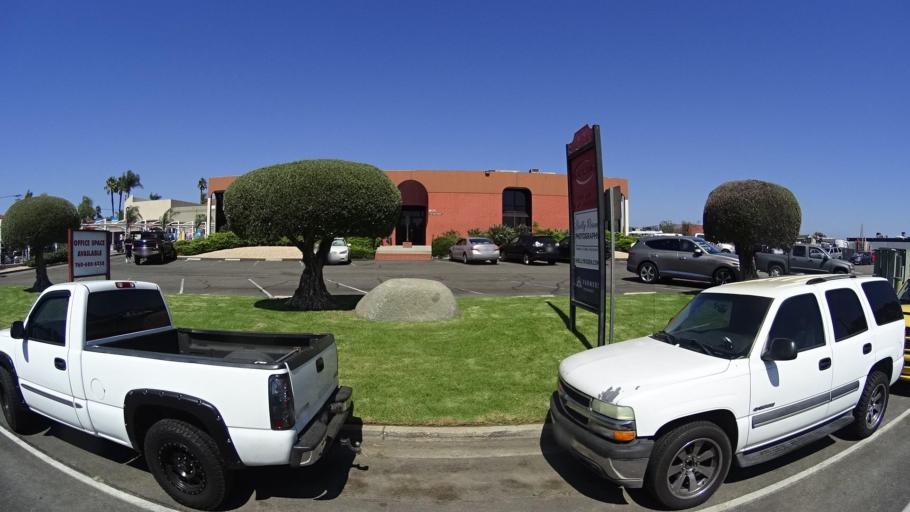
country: US
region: California
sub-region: San Diego County
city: Lake San Marcos
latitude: 33.1399
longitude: -117.2022
